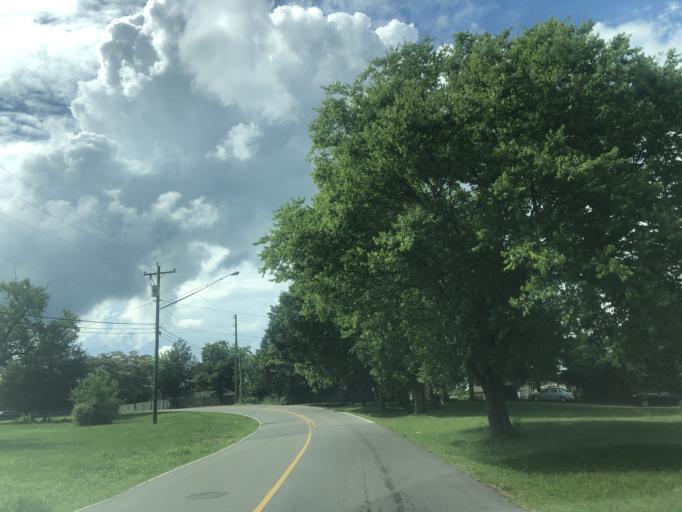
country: US
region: Tennessee
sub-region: Davidson County
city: Nashville
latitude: 36.2183
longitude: -86.8692
